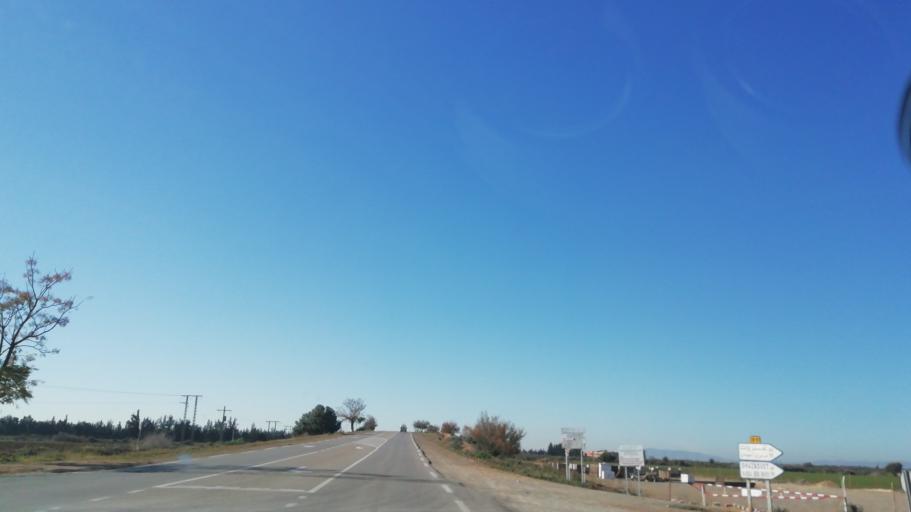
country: MA
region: Oriental
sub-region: Oujda-Angad
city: Oujda
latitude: 34.8096
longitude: -1.8155
